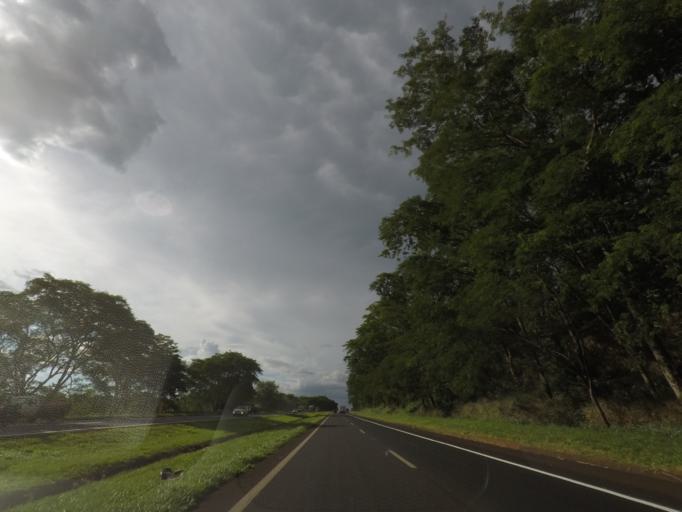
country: BR
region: Sao Paulo
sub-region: Jardinopolis
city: Jardinopolis
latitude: -21.0635
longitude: -47.8171
